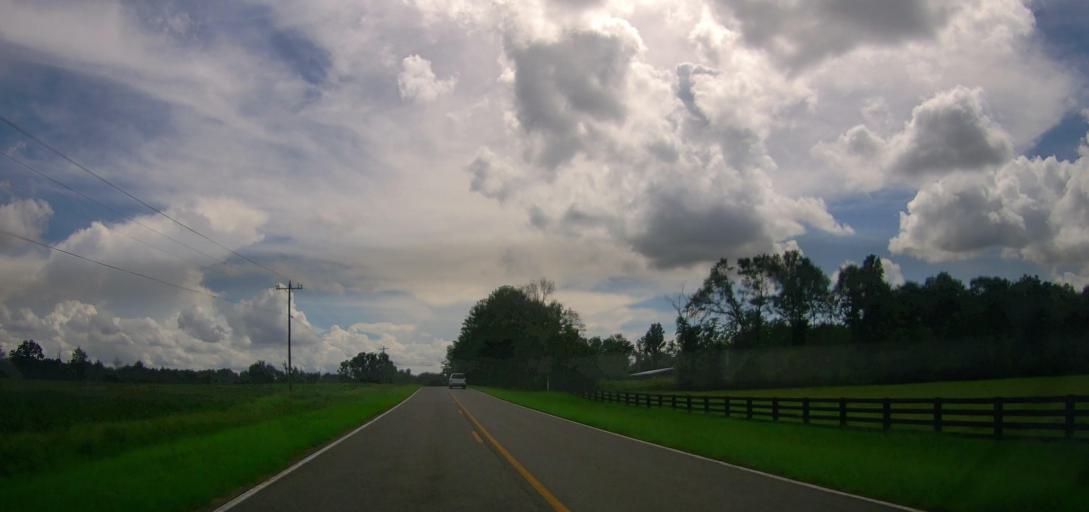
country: US
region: Georgia
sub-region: Taylor County
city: Butler
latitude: 32.4413
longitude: -84.1959
